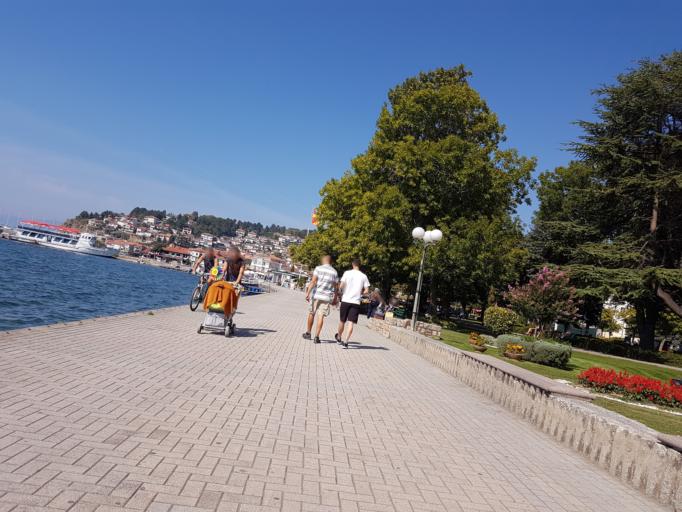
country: MK
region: Ohrid
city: Ohrid
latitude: 41.1116
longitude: 20.8014
